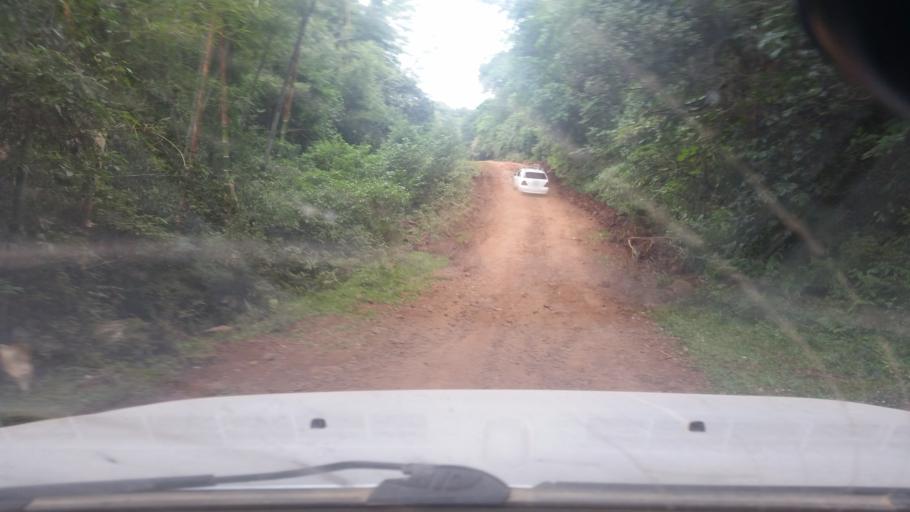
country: PY
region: Guaira
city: Independencia
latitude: -25.8164
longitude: -56.2751
